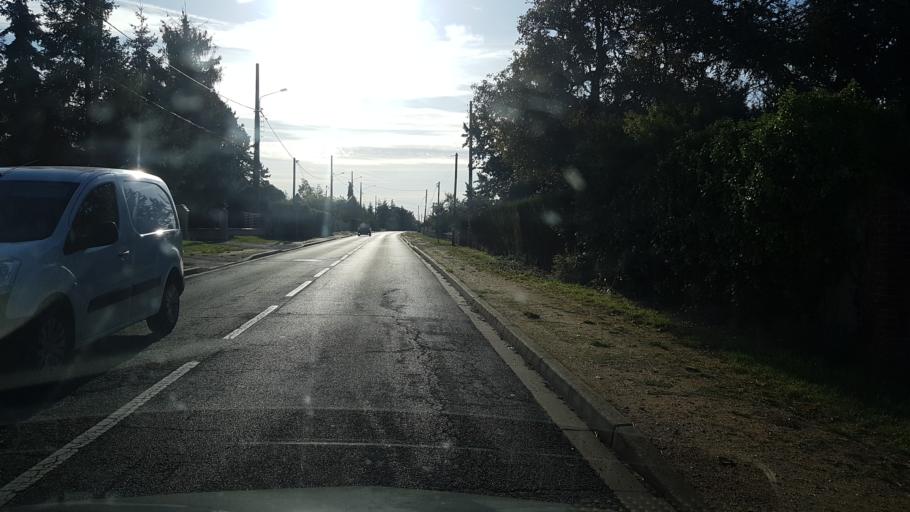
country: FR
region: Centre
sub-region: Departement du Loiret
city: Nevoy
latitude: 47.6960
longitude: 2.5488
